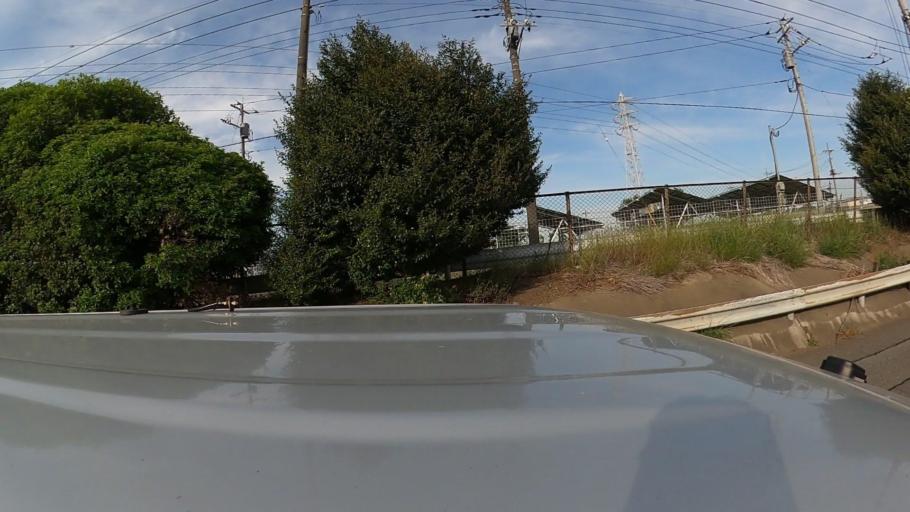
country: JP
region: Saitama
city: Oi
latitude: 35.8147
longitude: 139.5262
